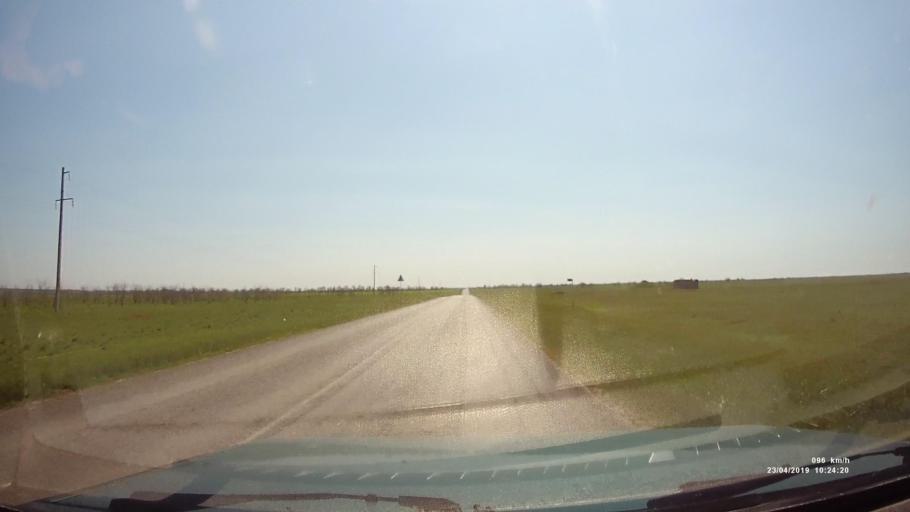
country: RU
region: Rostov
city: Sovetskoye
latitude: 46.6398
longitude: 42.4398
